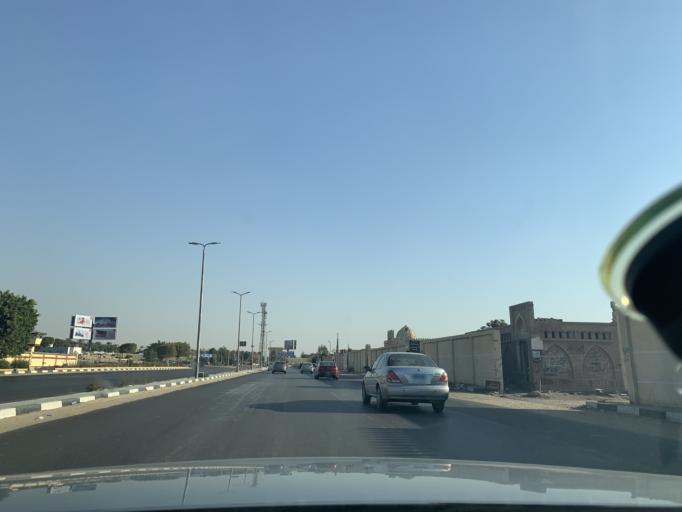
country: EG
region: Muhafazat al Qahirah
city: Cairo
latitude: 30.0273
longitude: 31.3539
